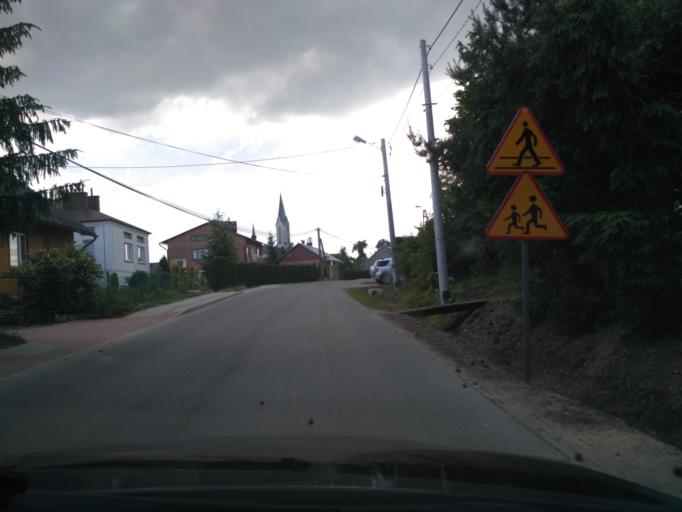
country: PL
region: Subcarpathian Voivodeship
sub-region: Powiat lancucki
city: Wysoka
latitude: 50.0470
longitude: 22.2526
